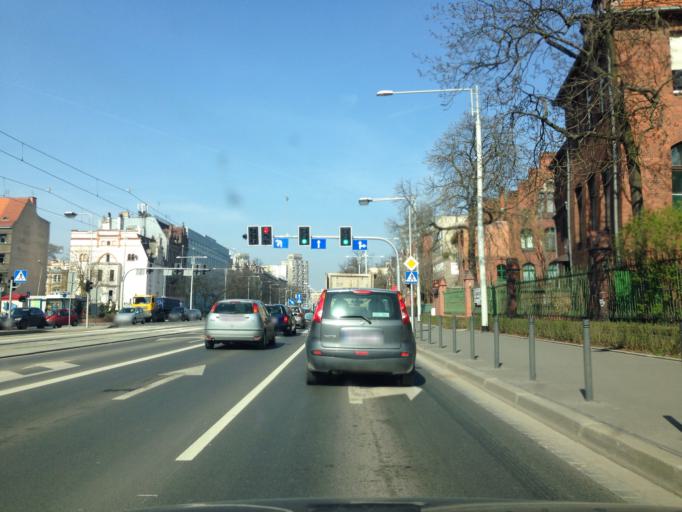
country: PL
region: Lower Silesian Voivodeship
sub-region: Powiat wroclawski
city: Wroclaw
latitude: 51.1093
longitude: 17.0666
